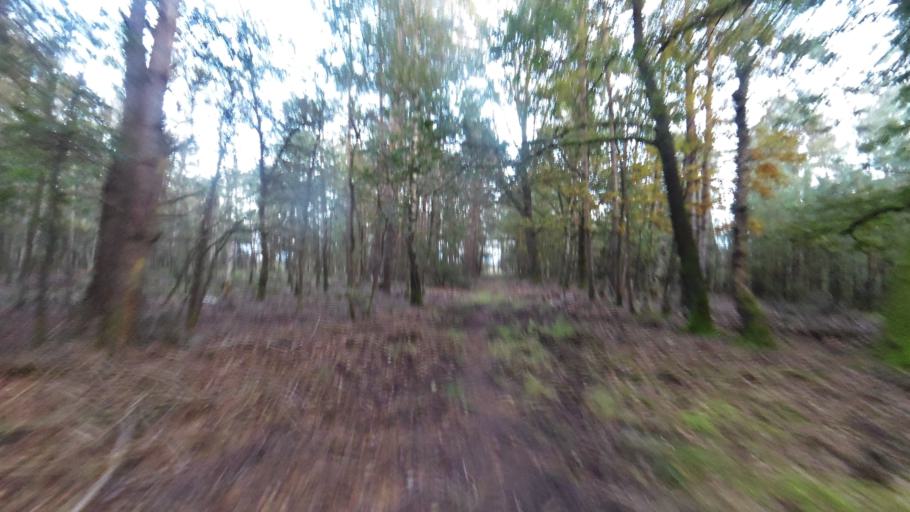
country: NL
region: Gelderland
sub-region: Gemeente Nunspeet
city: Nunspeet
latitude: 52.3287
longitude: 5.8000
